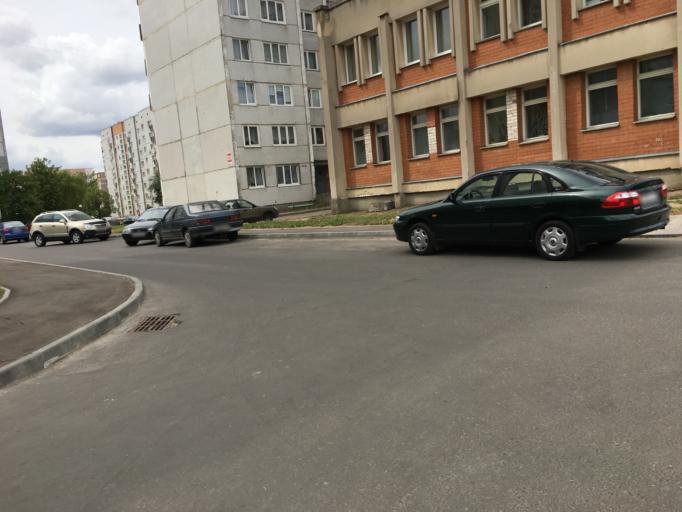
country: BY
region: Grodnenskaya
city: Hrodna
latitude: 53.7057
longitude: 23.8427
